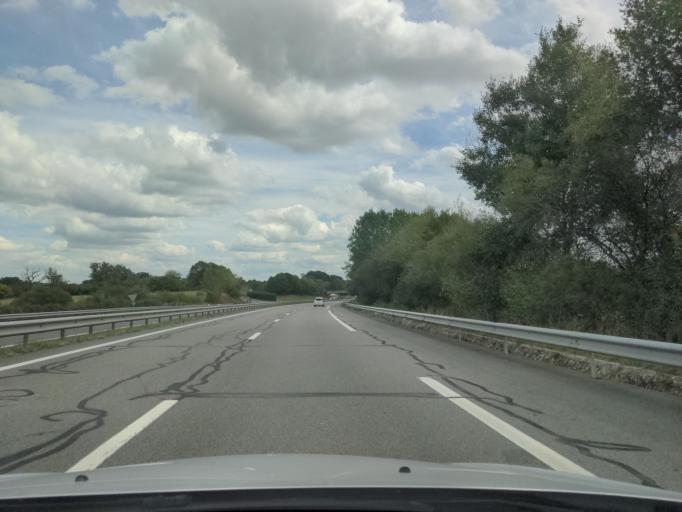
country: FR
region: Limousin
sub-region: Departement de la Creuse
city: Saint-Maurice-la-Souterraine
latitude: 46.2177
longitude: 1.4262
